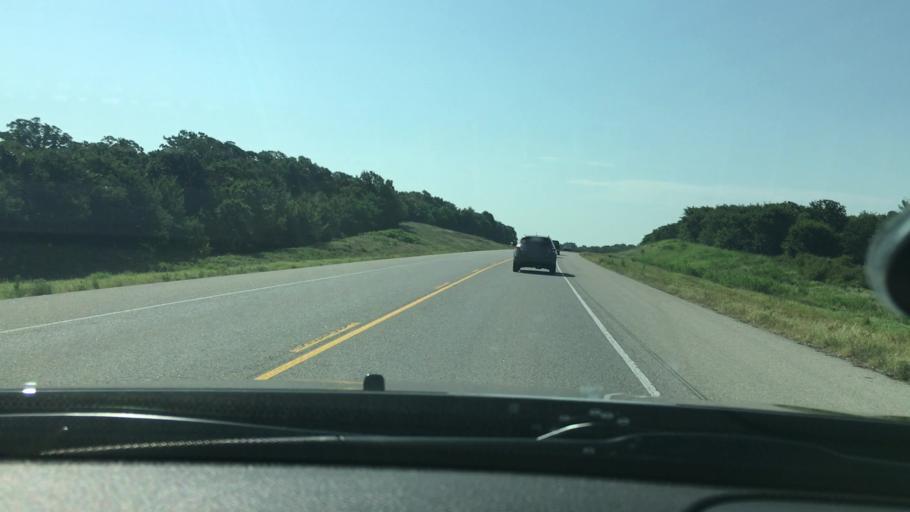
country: US
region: Oklahoma
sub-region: Pontotoc County
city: Ada
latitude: 34.6776
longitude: -96.5776
